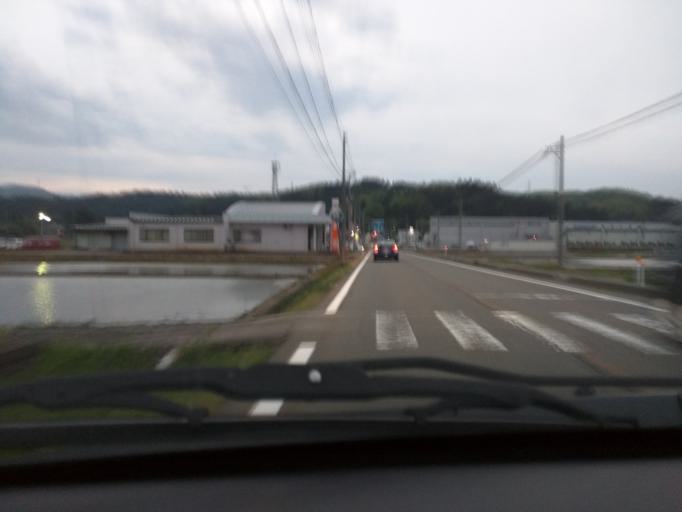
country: JP
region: Niigata
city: Ojiya
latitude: 37.3213
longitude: 138.7159
